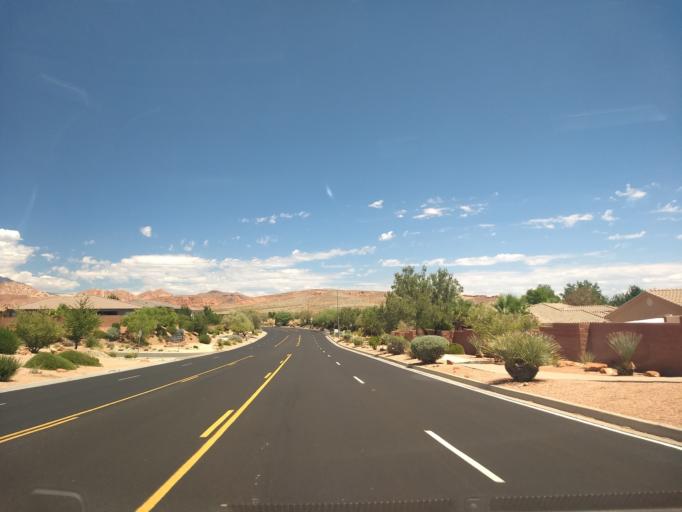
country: US
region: Utah
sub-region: Washington County
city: Washington
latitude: 37.1511
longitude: -113.5278
